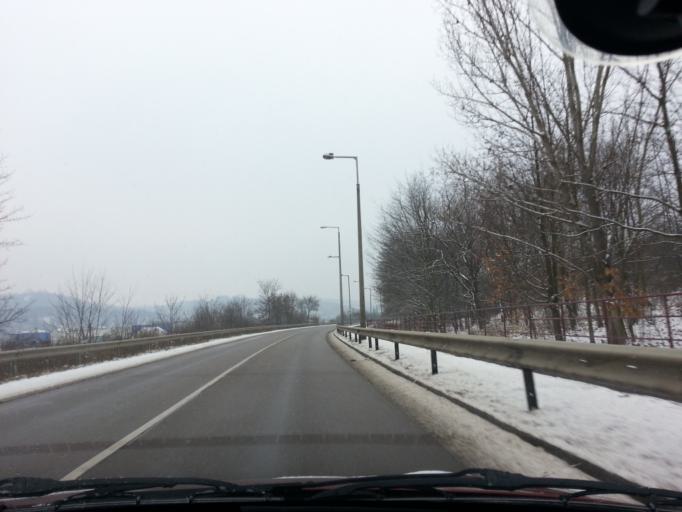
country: HU
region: Nograd
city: Salgotarjan
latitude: 48.0816
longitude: 19.7868
